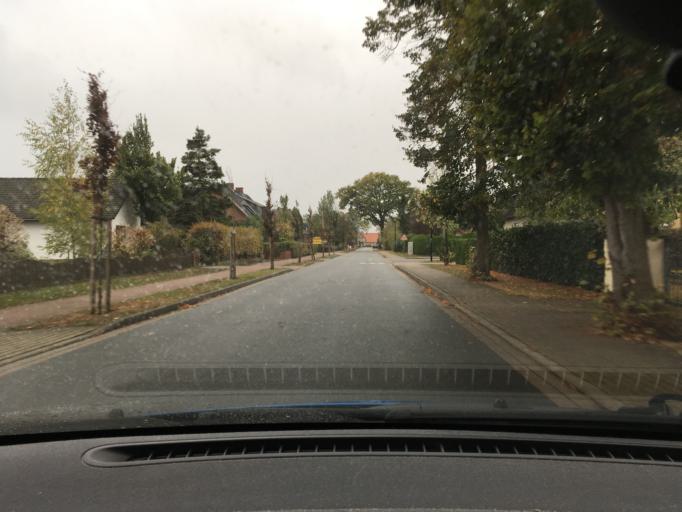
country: DE
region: Lower Saxony
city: Radbruch
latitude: 53.3138
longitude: 10.2879
